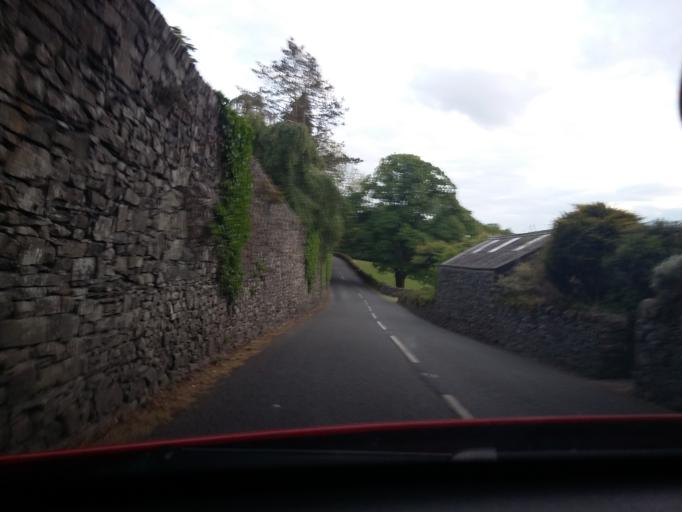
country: GB
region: England
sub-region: Cumbria
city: Windermere
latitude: 54.3941
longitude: -2.9149
